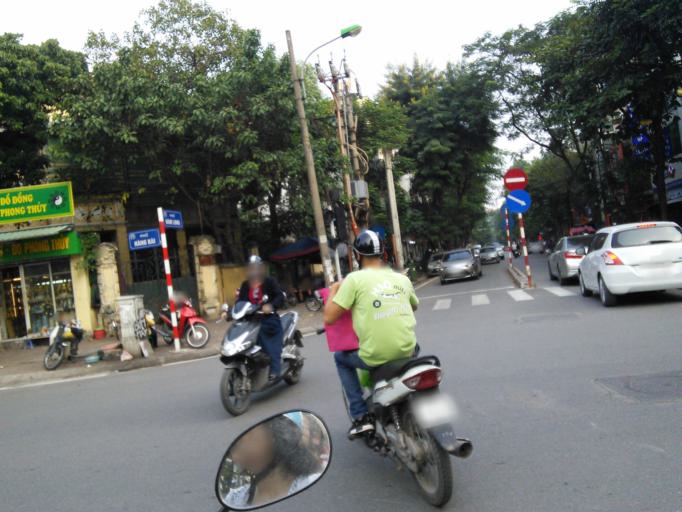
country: VN
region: Ha Noi
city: Hai BaTrung
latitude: 21.0198
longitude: 105.8519
